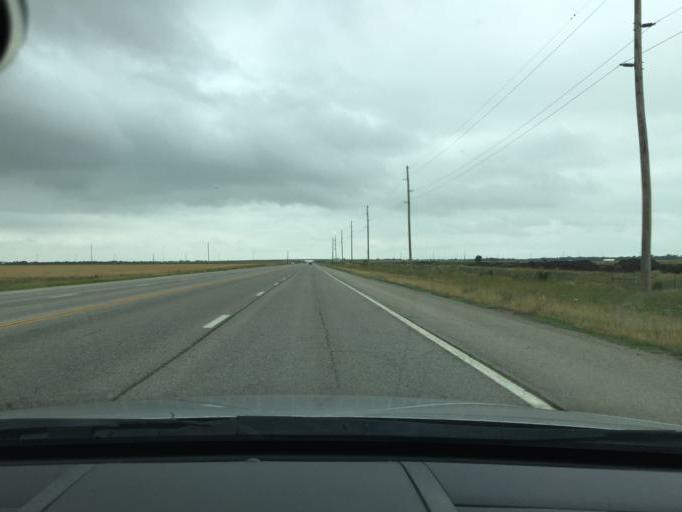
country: US
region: Kansas
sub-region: Reno County
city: Hutchinson
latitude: 38.0397
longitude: -97.8669
